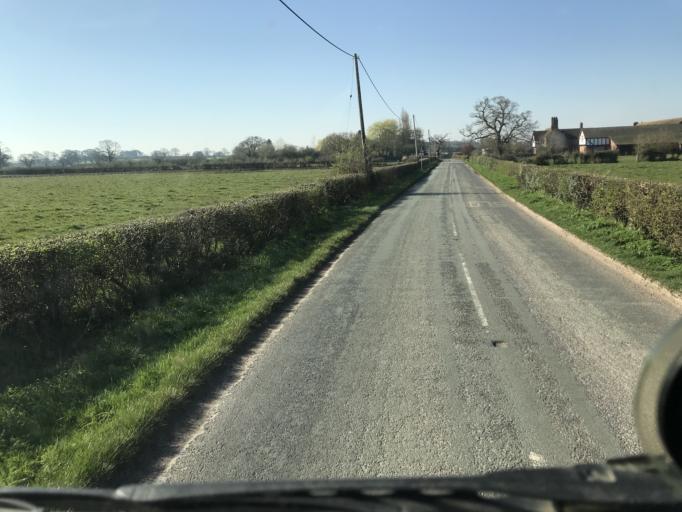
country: GB
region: England
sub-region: Cheshire West and Chester
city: Waverton
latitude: 53.1630
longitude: -2.8260
